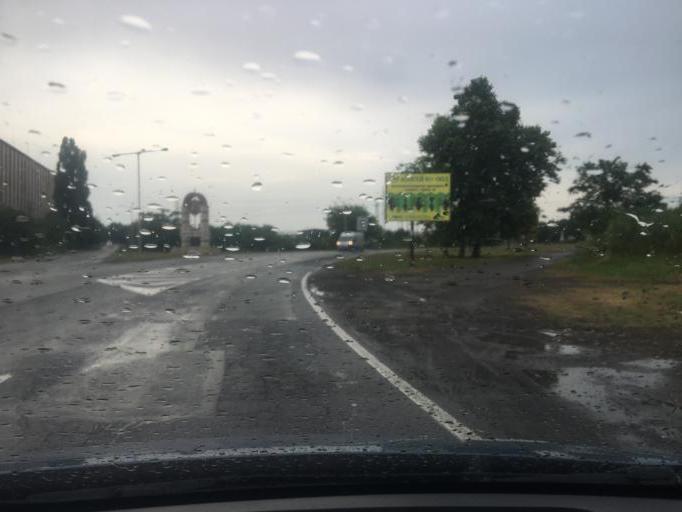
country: BG
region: Burgas
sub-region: Obshtina Pomorie
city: Pomorie
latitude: 42.5787
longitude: 27.6056
